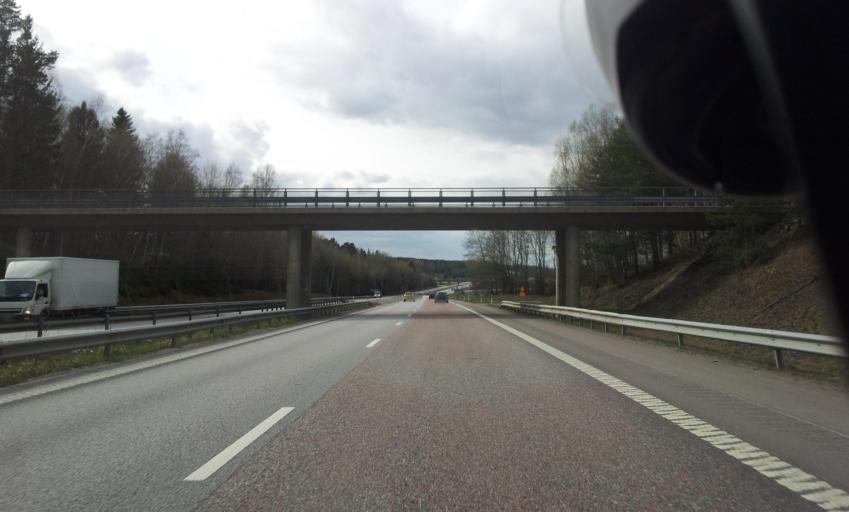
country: SE
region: Uppsala
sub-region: Habo Kommun
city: Balsta
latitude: 59.5825
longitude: 17.5228
